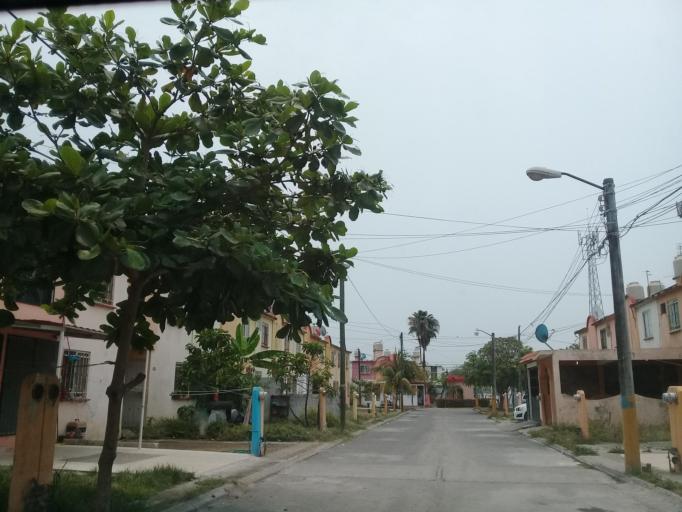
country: MX
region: Veracruz
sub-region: Veracruz
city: Las Amapolas
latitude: 19.1510
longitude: -96.2041
